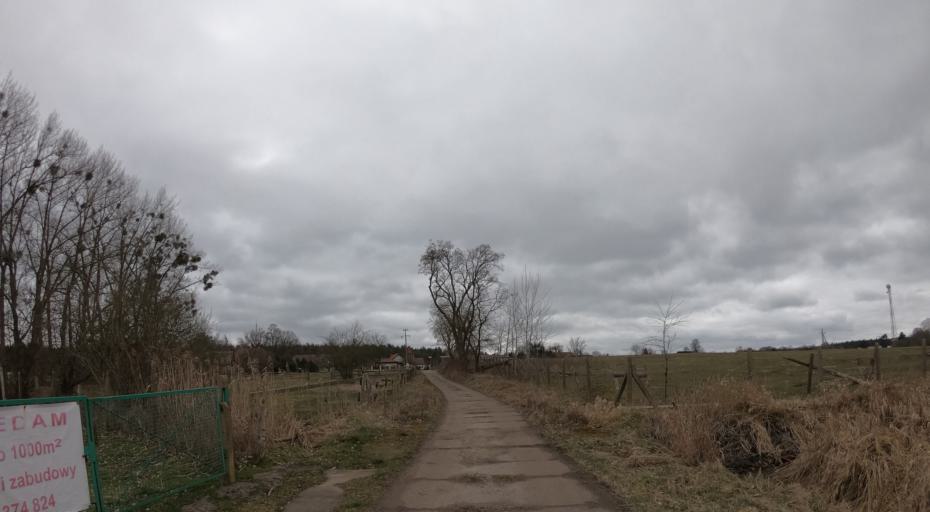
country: PL
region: West Pomeranian Voivodeship
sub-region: Powiat policki
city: Nowe Warpno
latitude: 53.6767
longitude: 14.3831
